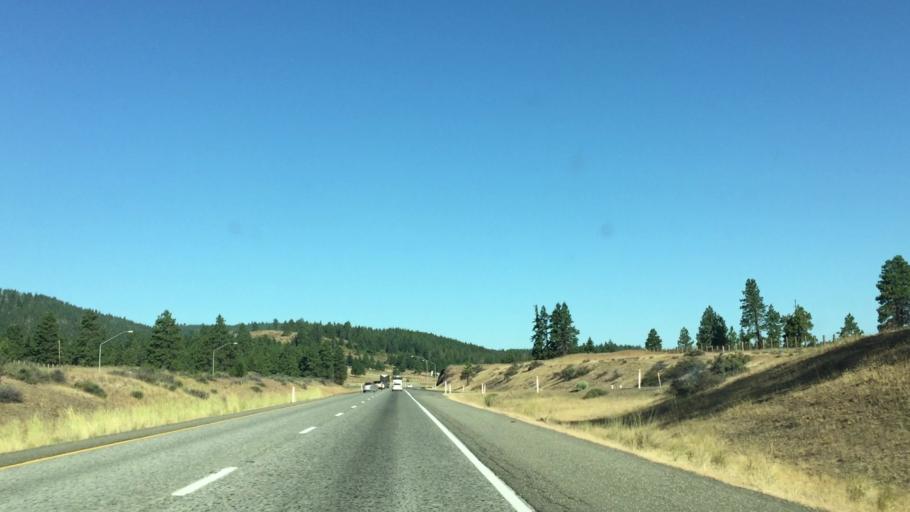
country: US
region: Washington
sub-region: Kittitas County
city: Cle Elum
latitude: 47.1150
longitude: -120.7916
